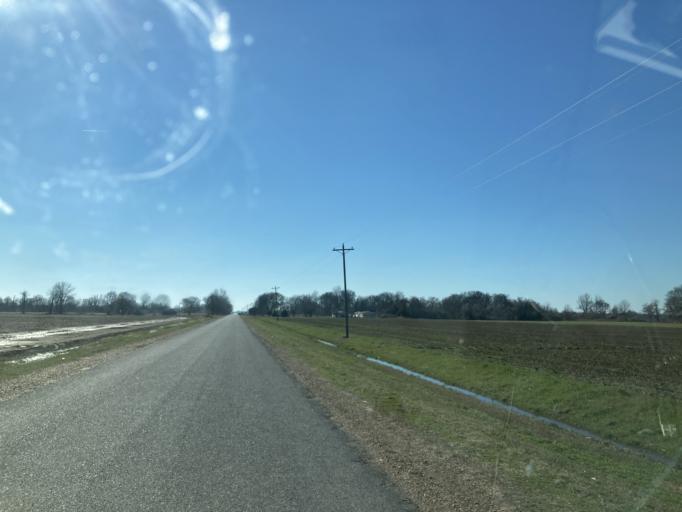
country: US
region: Mississippi
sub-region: Yazoo County
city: Yazoo City
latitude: 32.9730
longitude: -90.5947
